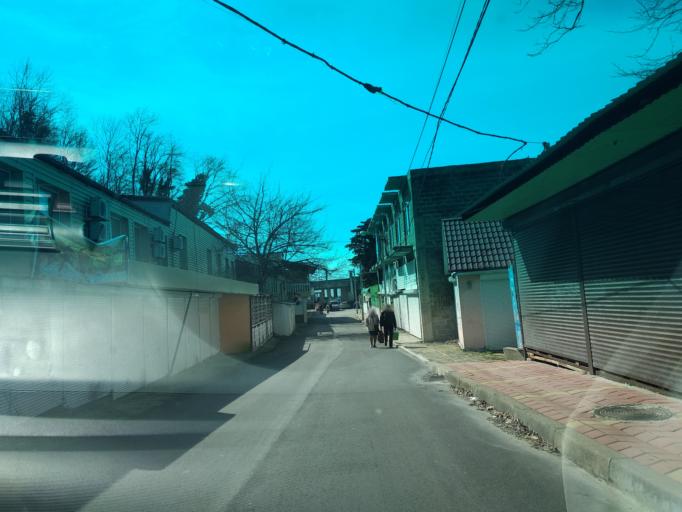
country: RU
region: Krasnodarskiy
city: Shepsi
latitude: 44.0321
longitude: 39.1455
